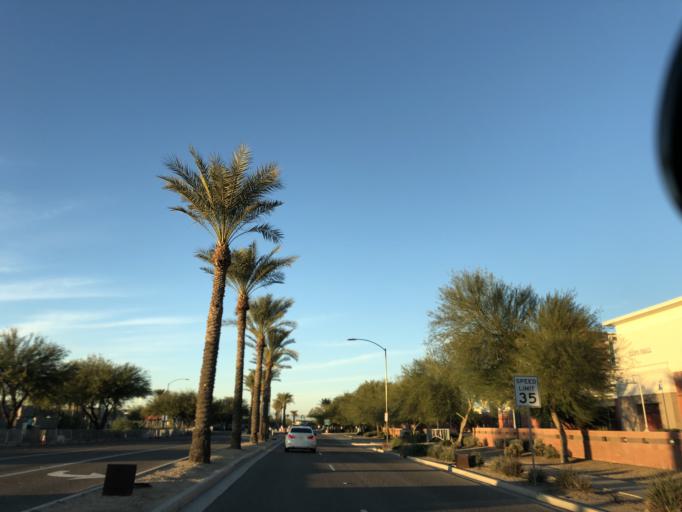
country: US
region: Arizona
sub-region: Maricopa County
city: Peoria
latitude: 33.5304
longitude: -112.2647
